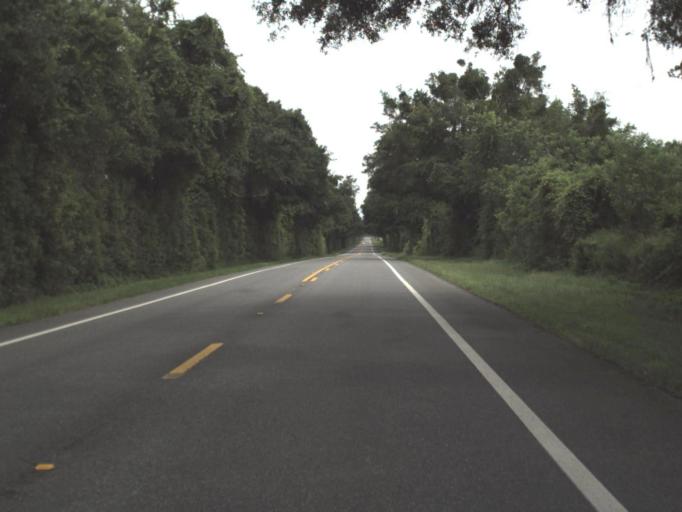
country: US
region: Florida
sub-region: Alachua County
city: Archer
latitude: 29.5726
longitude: -82.5451
